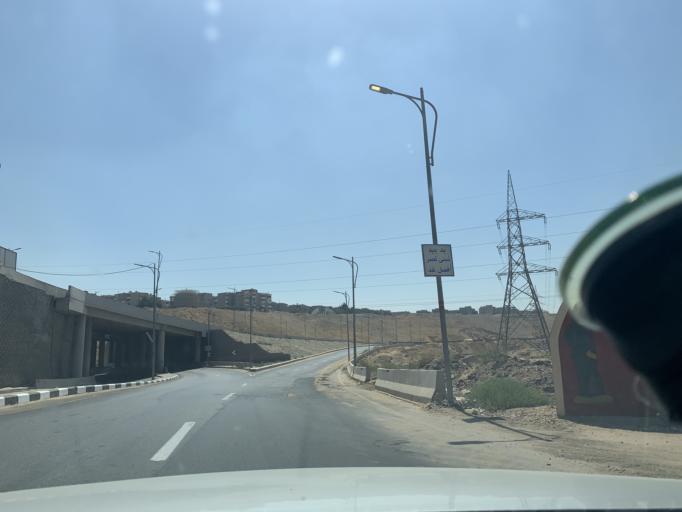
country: EG
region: Muhafazat al Qahirah
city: Cairo
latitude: 30.0151
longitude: 31.3428
